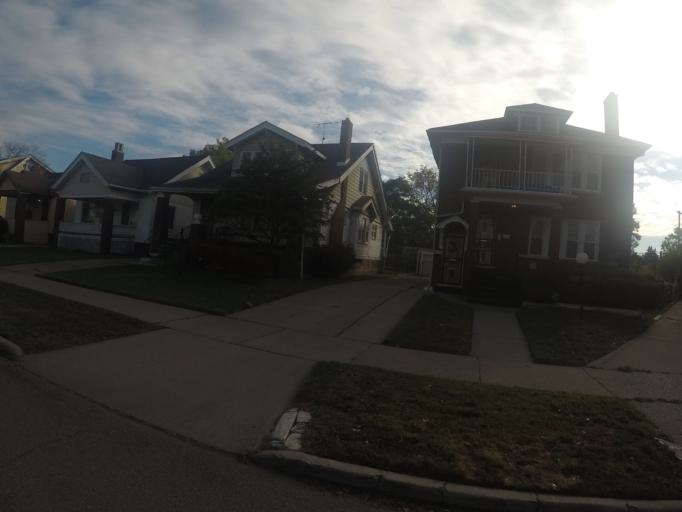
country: US
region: Michigan
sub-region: Wayne County
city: Highland Park
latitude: 42.3652
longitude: -83.1374
